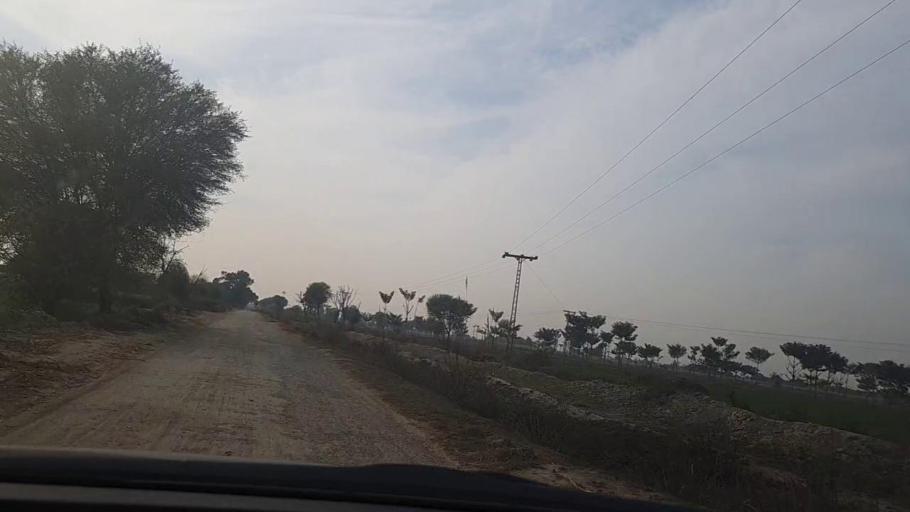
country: PK
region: Sindh
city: Daulatpur
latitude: 26.3340
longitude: 68.0636
